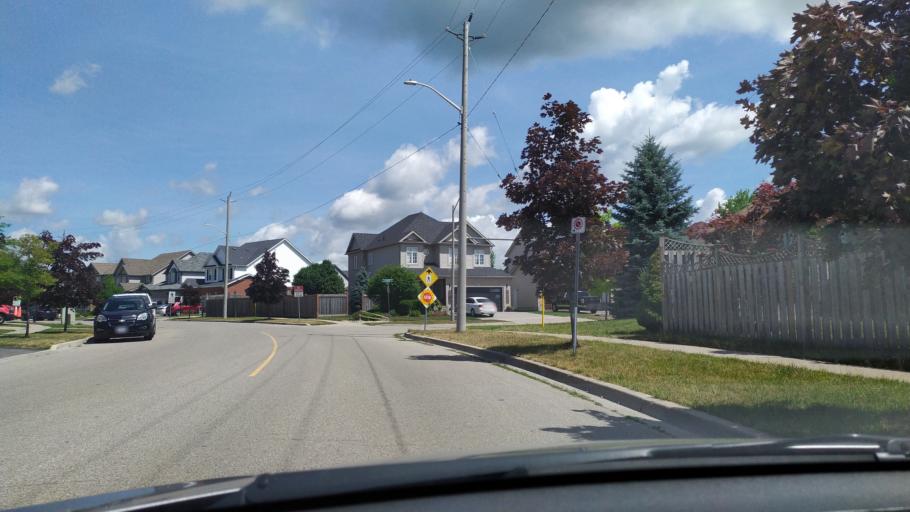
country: CA
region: Ontario
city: Kitchener
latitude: 43.4080
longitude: -80.6706
